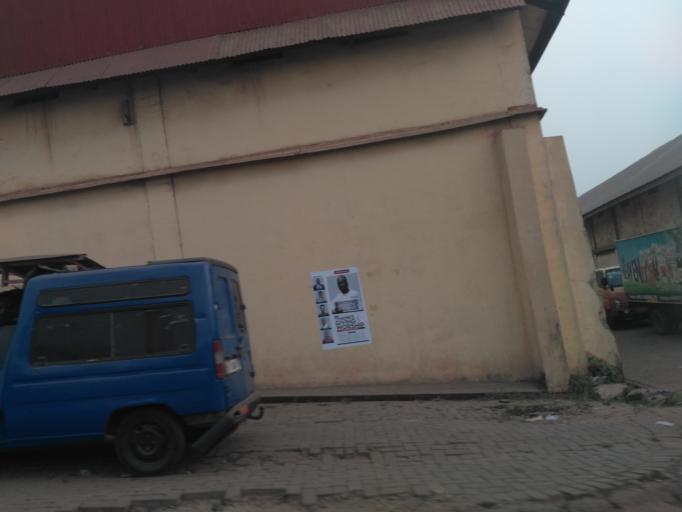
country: GH
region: Ashanti
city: Kumasi
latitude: 6.6812
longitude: -1.6154
